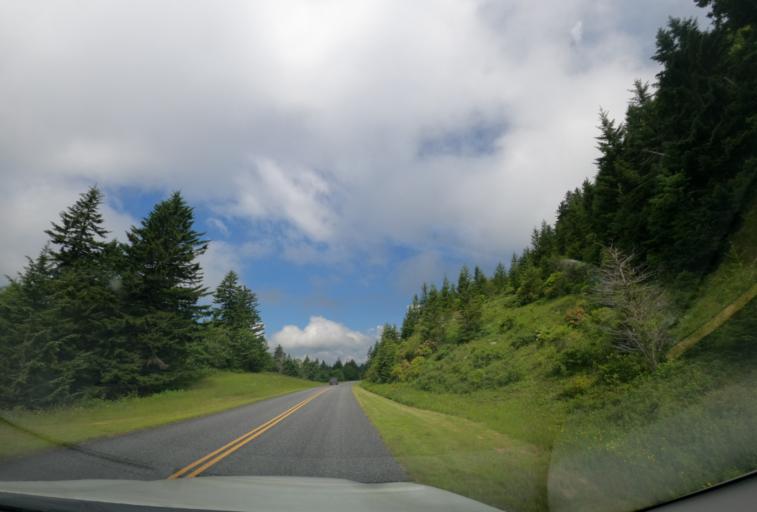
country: US
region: North Carolina
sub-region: Haywood County
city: Hazelwood
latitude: 35.3662
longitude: -82.9941
